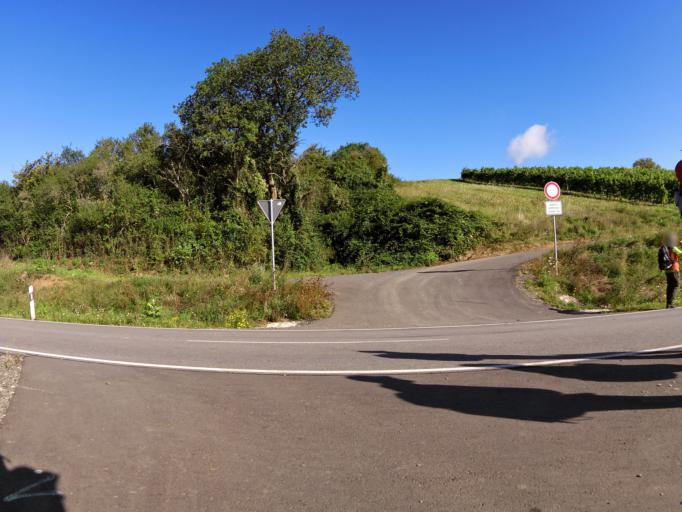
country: DE
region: Rheinland-Pfalz
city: Waldbockelheim
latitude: 49.8194
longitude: 7.7156
